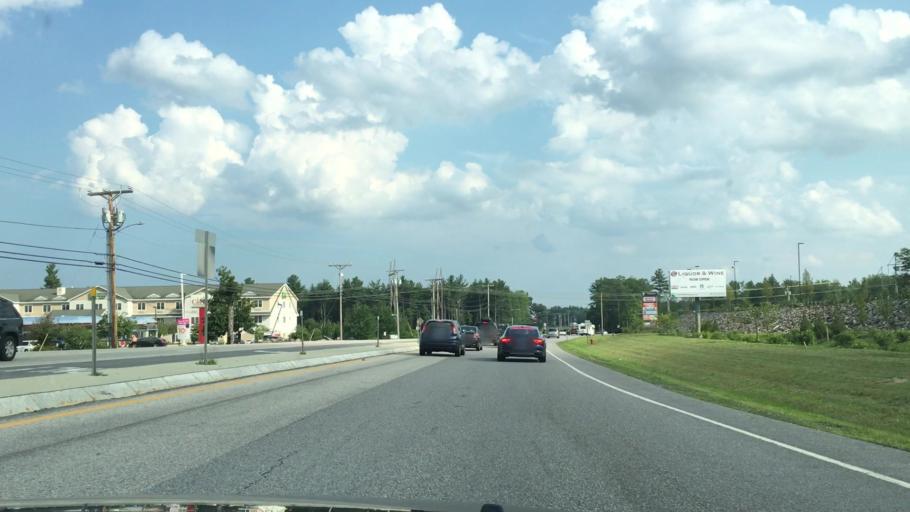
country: US
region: New Hampshire
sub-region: Strafford County
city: Rochester
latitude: 43.3337
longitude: -71.0083
